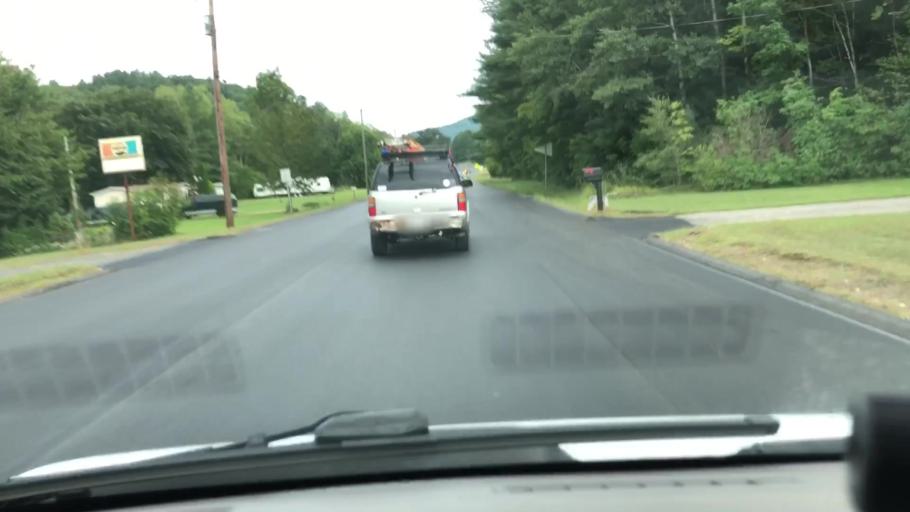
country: US
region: Massachusetts
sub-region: Franklin County
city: Charlemont
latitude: 42.6415
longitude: -72.9162
